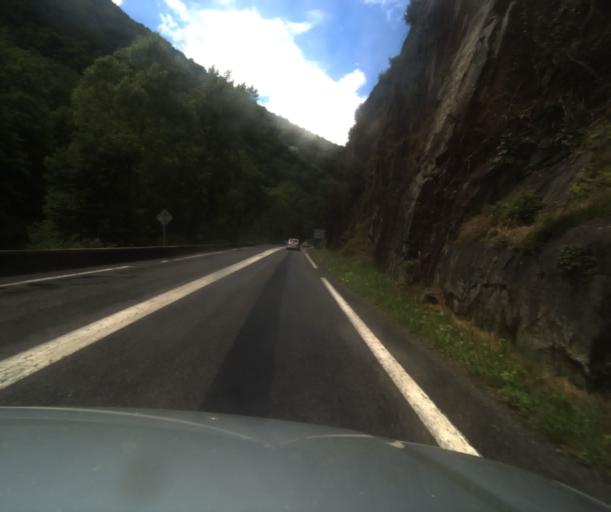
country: FR
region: Midi-Pyrenees
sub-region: Departement des Hautes-Pyrenees
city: Pierrefitte-Nestalas
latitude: 42.9503
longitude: -0.0659
